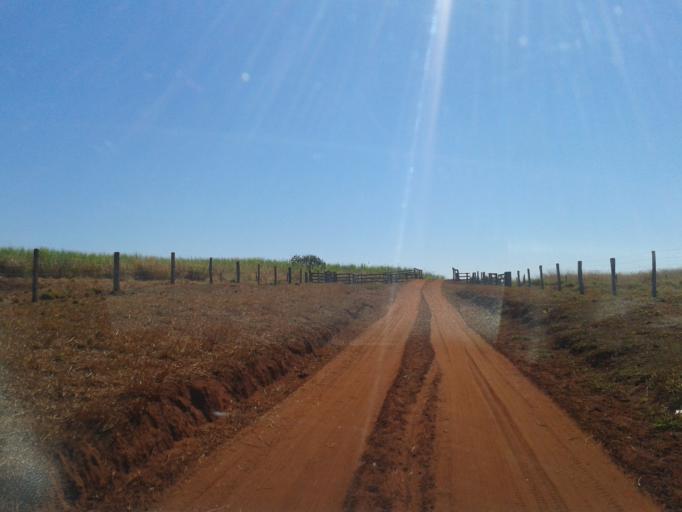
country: BR
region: Minas Gerais
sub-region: Santa Vitoria
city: Santa Vitoria
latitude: -19.1503
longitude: -50.2041
